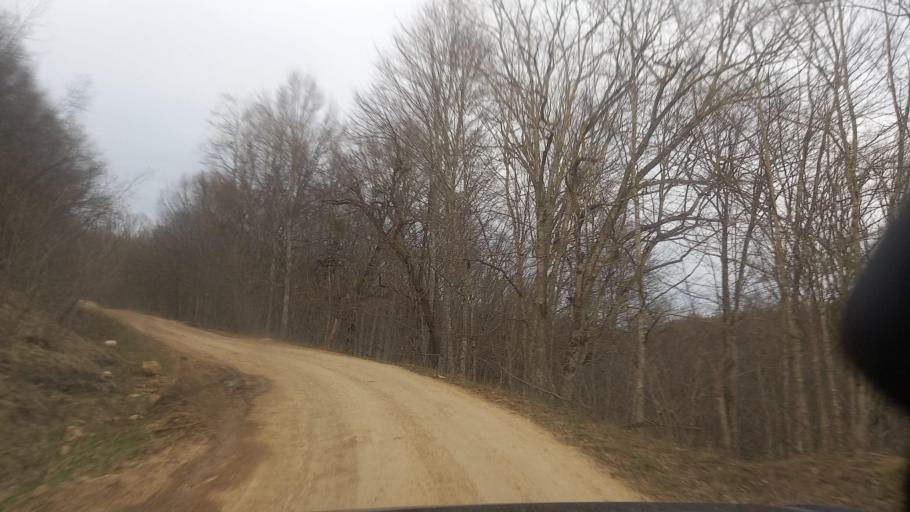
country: RU
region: Adygeya
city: Kamennomostskiy
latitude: 44.2079
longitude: 40.0050
